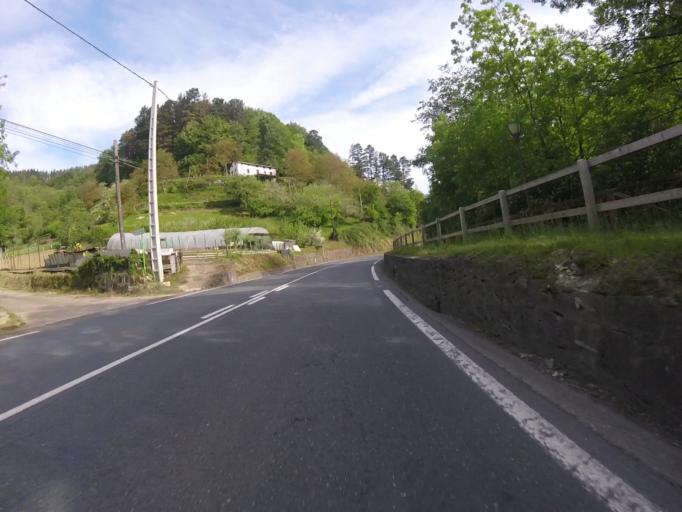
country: ES
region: Basque Country
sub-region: Provincia de Guipuzcoa
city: Urretxu
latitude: 43.1015
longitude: -2.3178
